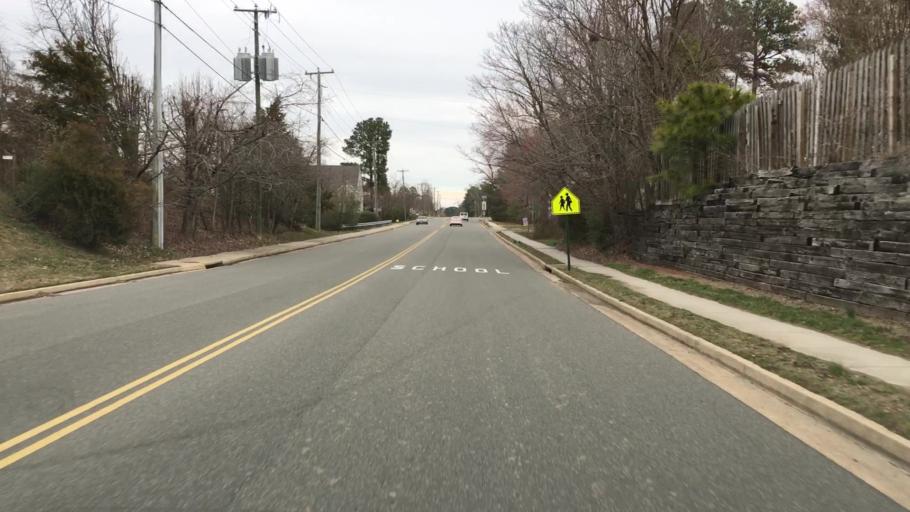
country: US
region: Virginia
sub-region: Henrico County
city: Laurel
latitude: 37.6567
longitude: -77.5457
